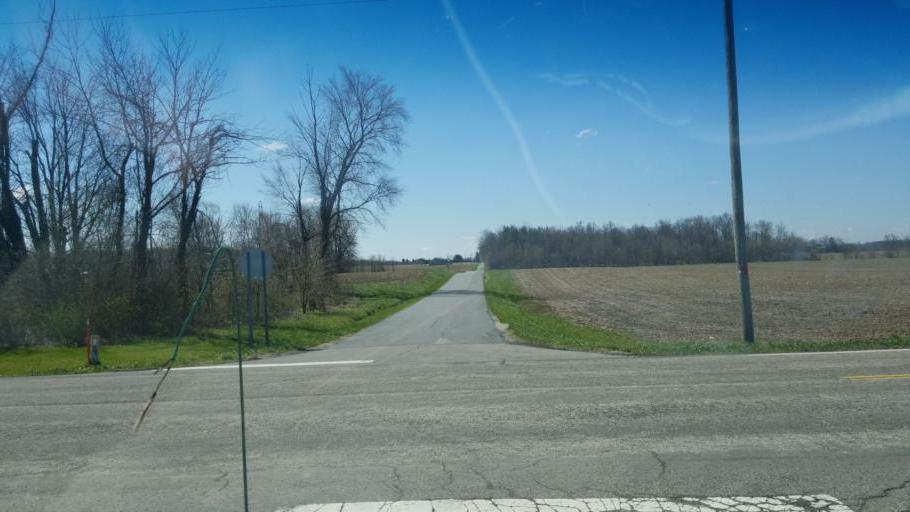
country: US
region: Ohio
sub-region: Crawford County
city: Crestline
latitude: 40.8579
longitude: -82.8180
